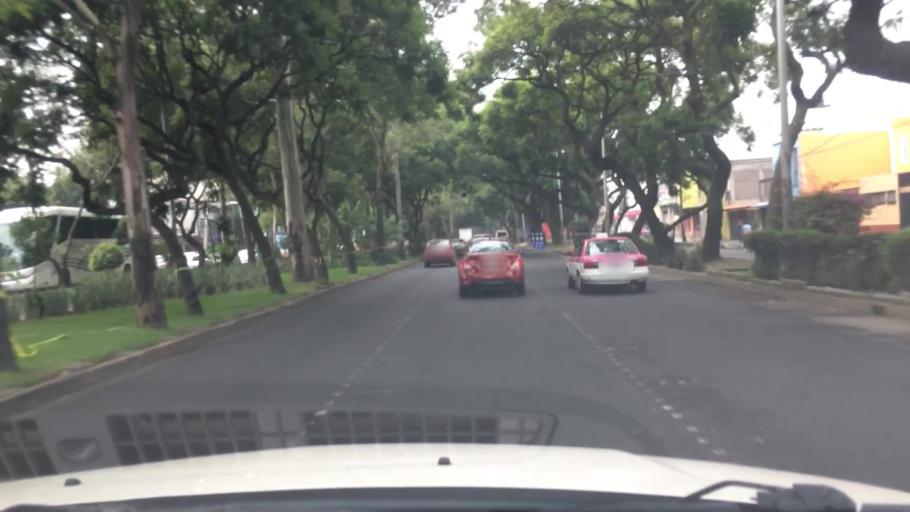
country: MX
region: Mexico City
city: Coyoacan
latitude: 19.3293
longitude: -99.1370
